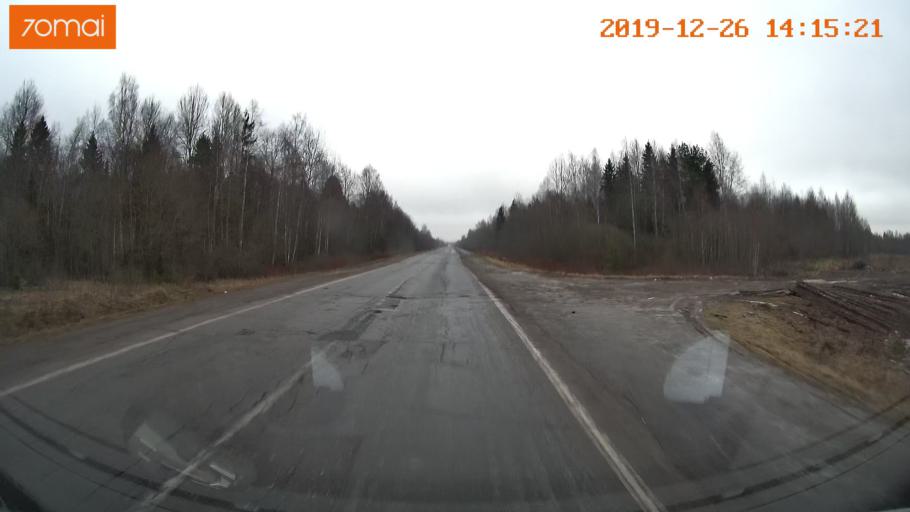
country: RU
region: Jaroslavl
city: Poshekhon'ye
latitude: 58.5153
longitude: 39.0433
